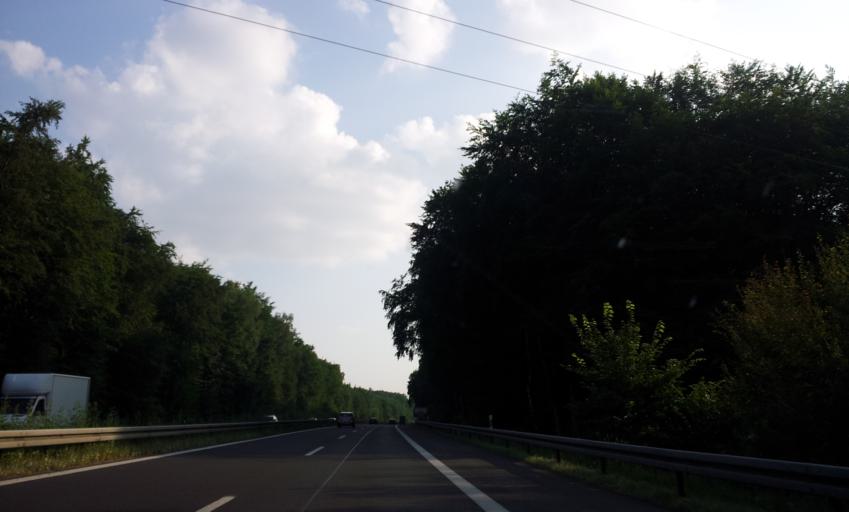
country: DE
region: Brandenburg
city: Gramzow
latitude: 53.1684
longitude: 13.9182
